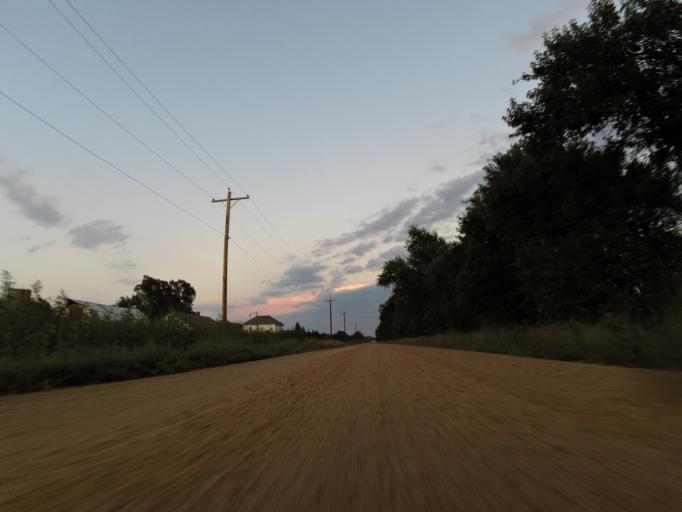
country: US
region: Kansas
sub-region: Reno County
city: South Hutchinson
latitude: 37.9556
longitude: -98.0494
